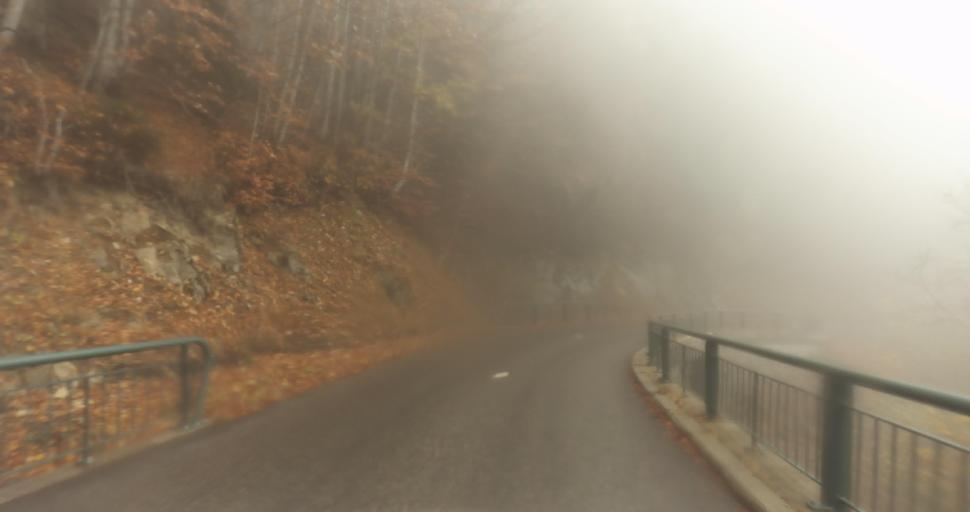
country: FR
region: Rhone-Alpes
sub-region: Departement de la Haute-Savoie
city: Thorens-Glieres
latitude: 45.9617
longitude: 6.3014
